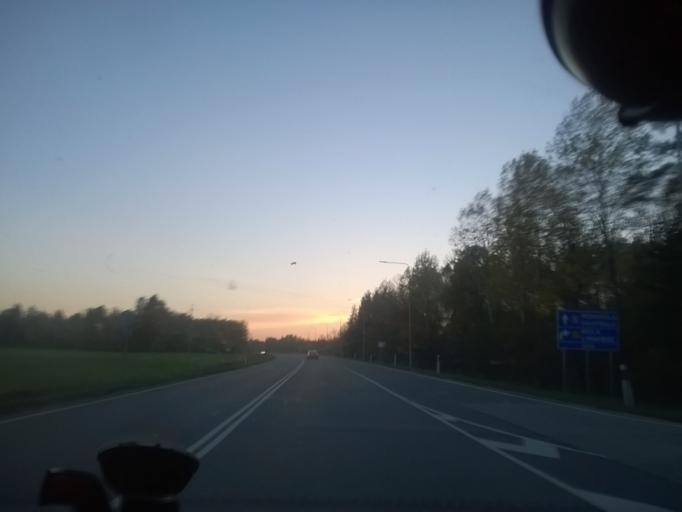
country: EE
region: Laeaene
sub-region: Ridala Parish
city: Uuemoisa
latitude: 58.9591
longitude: 23.6728
